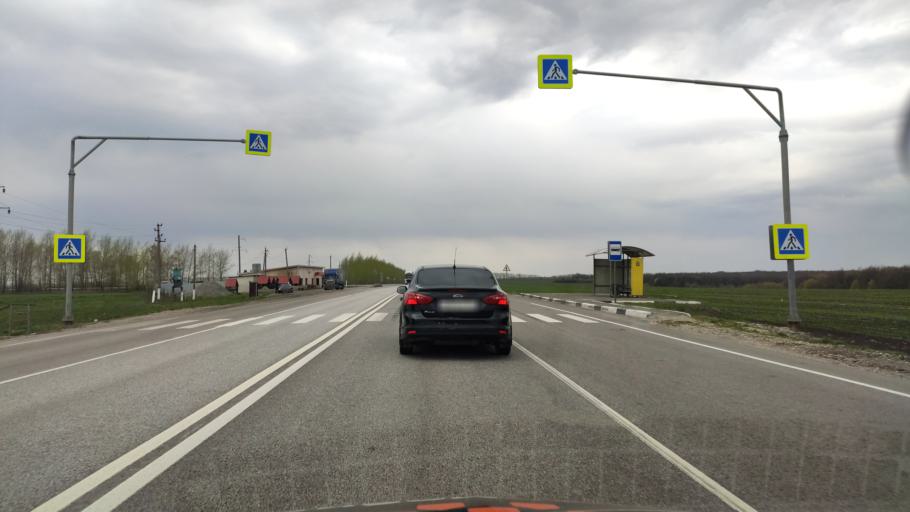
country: RU
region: Voronezj
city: Nizhnedevitsk
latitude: 51.5845
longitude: 38.5423
